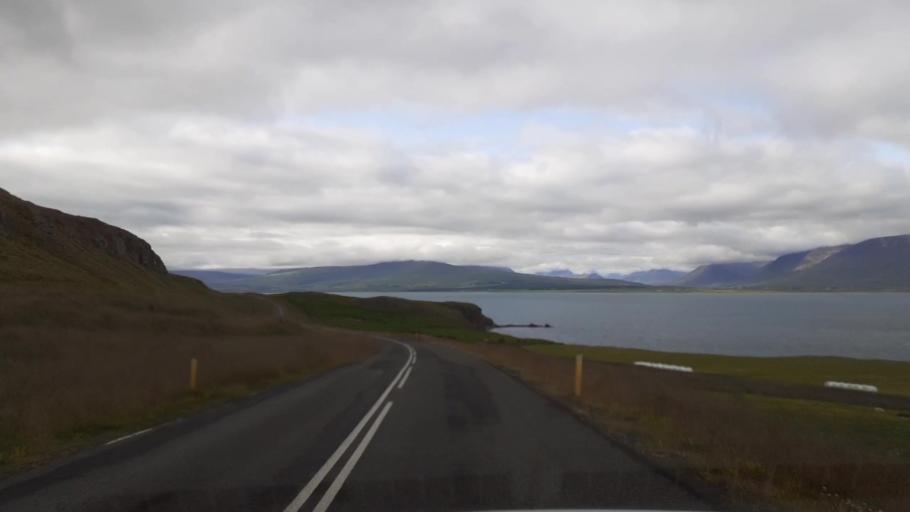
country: IS
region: Northeast
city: Akureyri
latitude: 65.8137
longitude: -18.0504
